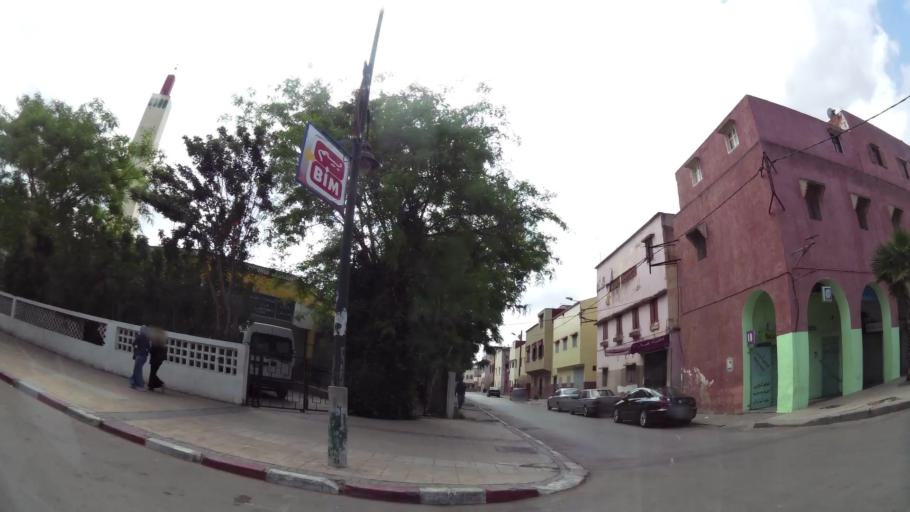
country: MA
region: Gharb-Chrarda-Beni Hssen
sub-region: Kenitra Province
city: Kenitra
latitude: 34.2598
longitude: -6.5644
